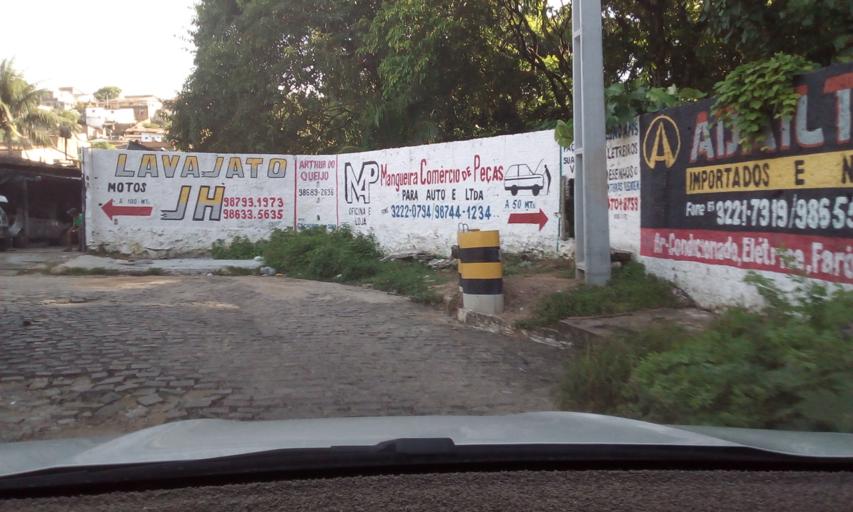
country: BR
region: Paraiba
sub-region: Joao Pessoa
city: Joao Pessoa
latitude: -7.1337
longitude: -34.8881
